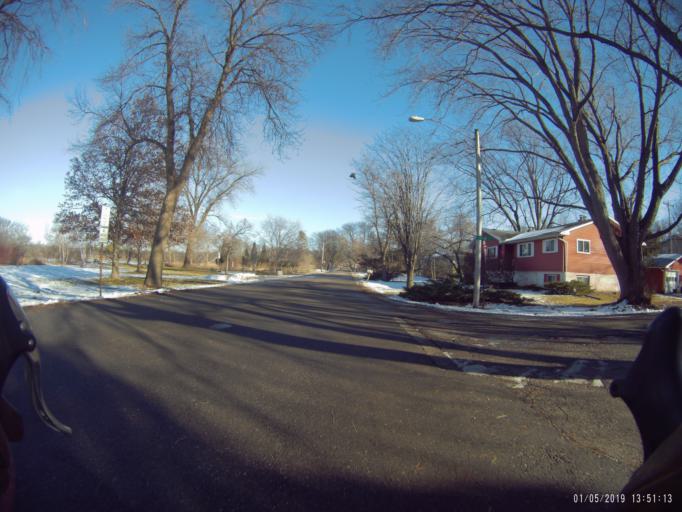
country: US
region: Wisconsin
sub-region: Dane County
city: Madison
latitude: 43.0447
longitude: -89.4115
